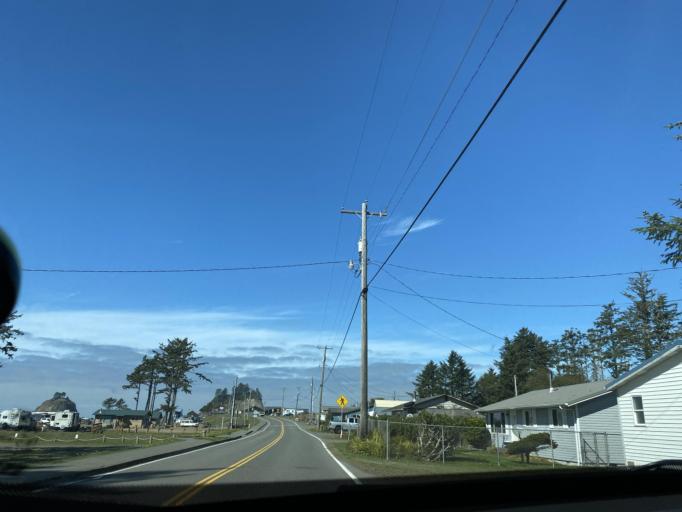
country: US
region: Washington
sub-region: Clallam County
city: Forks
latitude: 47.9066
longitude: -124.6330
